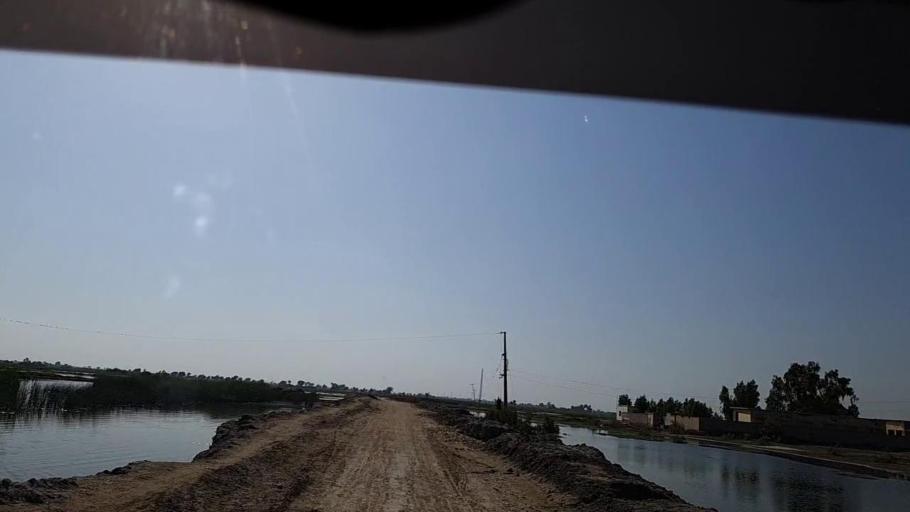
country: PK
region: Sindh
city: Tangwani
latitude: 28.3610
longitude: 69.0269
